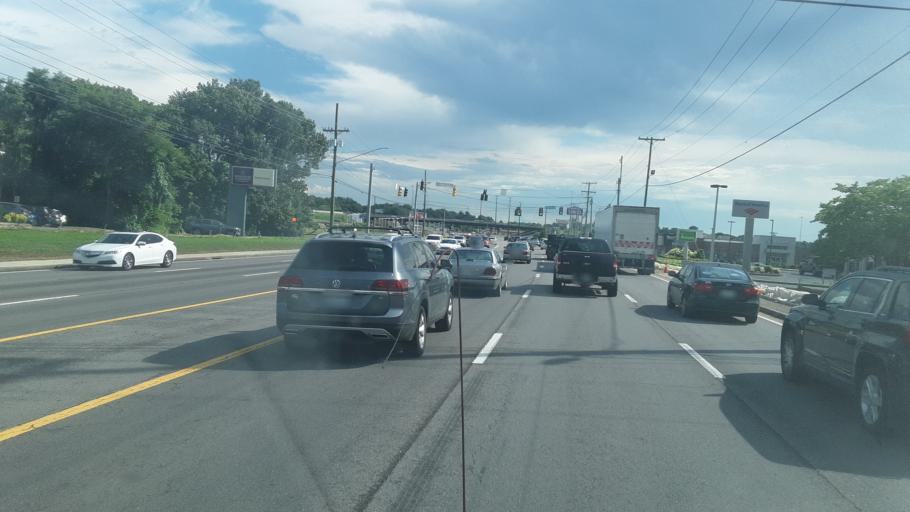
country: US
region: Tennessee
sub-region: Montgomery County
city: Clarksville
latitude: 36.5772
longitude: -87.3012
